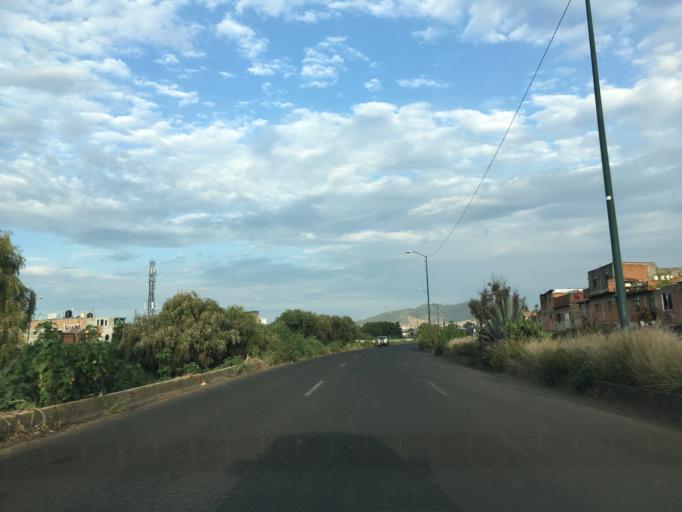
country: MX
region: Michoacan
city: Morelia
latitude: 19.7145
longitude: -101.2040
